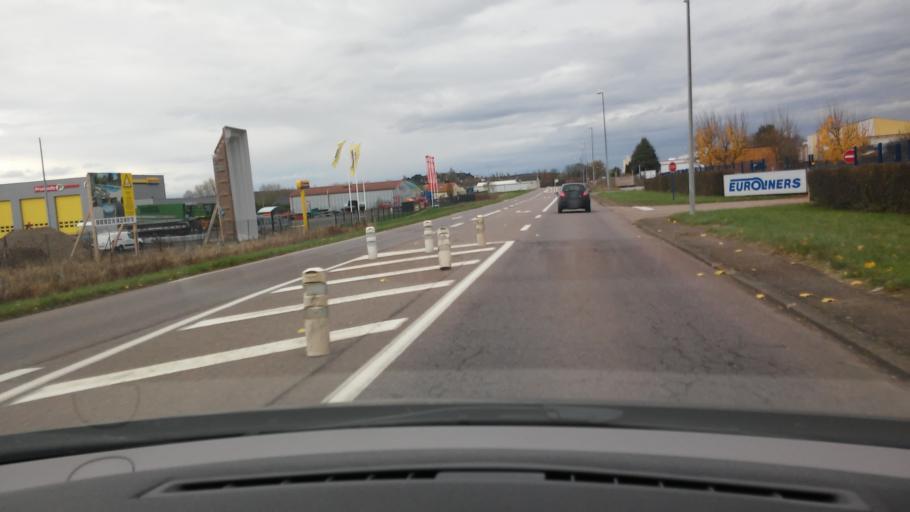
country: FR
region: Lorraine
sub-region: Departement de la Moselle
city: Boulay-Moselle
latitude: 49.1778
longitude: 6.4719
